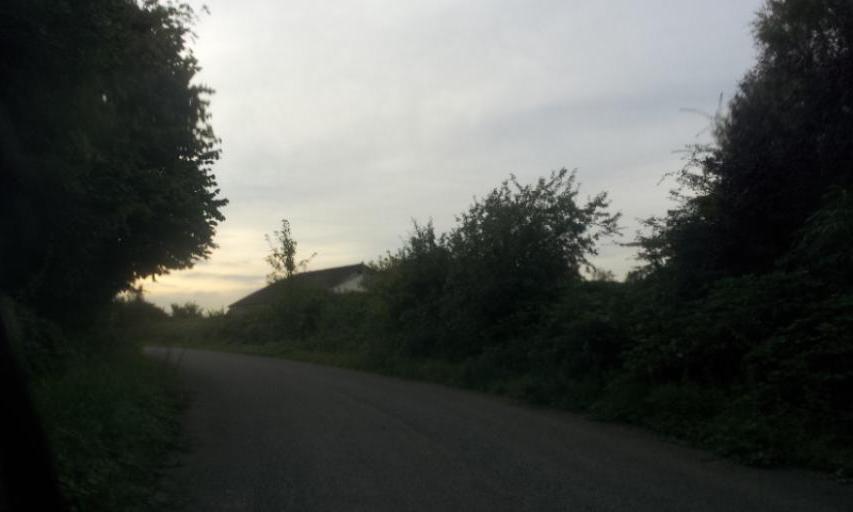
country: GB
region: England
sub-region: Kent
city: Boxley
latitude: 51.3011
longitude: 0.5155
